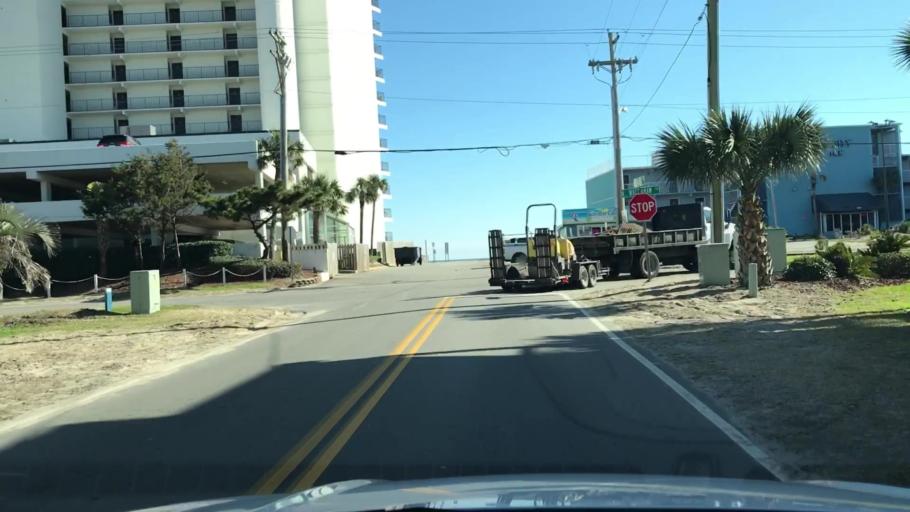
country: US
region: South Carolina
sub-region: Horry County
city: Garden City
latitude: 33.5857
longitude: -78.9912
